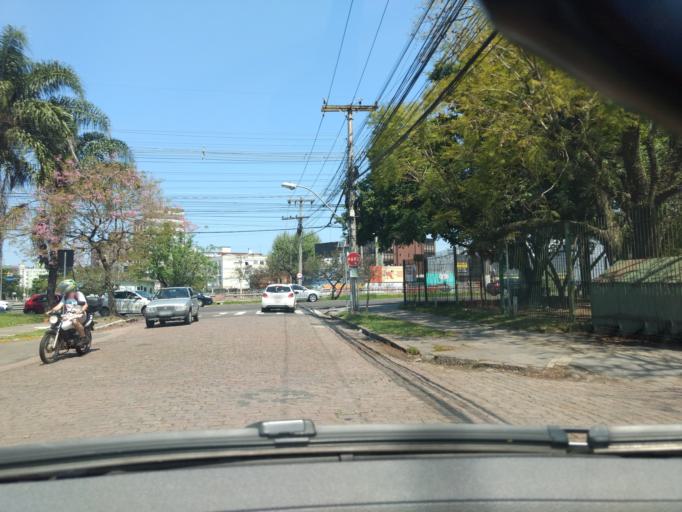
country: BR
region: Rio Grande do Sul
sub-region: Porto Alegre
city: Porto Alegre
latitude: -30.0427
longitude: -51.2052
